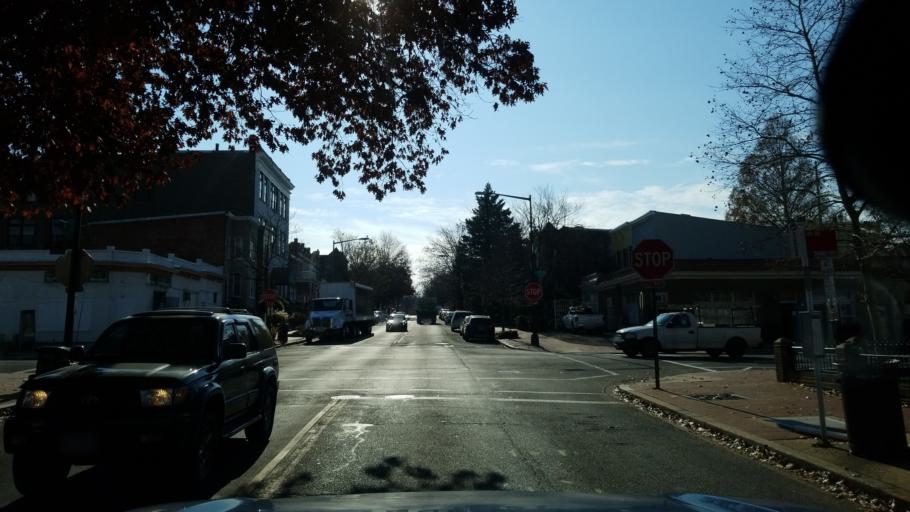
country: US
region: Washington, D.C.
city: Washington, D.C.
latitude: 38.8976
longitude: -76.9950
